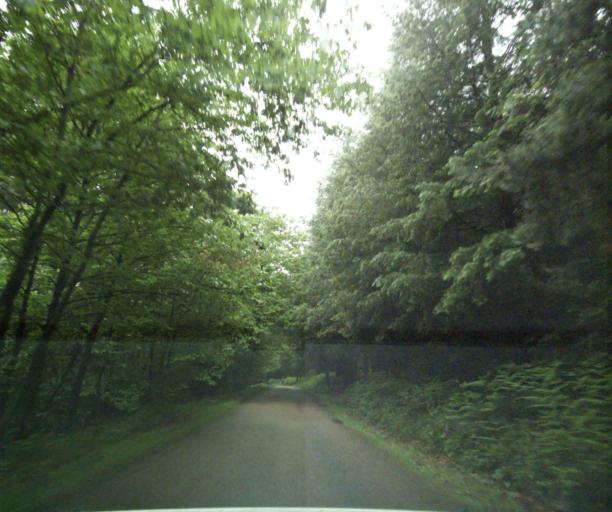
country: FR
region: Bourgogne
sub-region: Departement de Saone-et-Loire
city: Charolles
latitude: 46.4037
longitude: 4.3623
